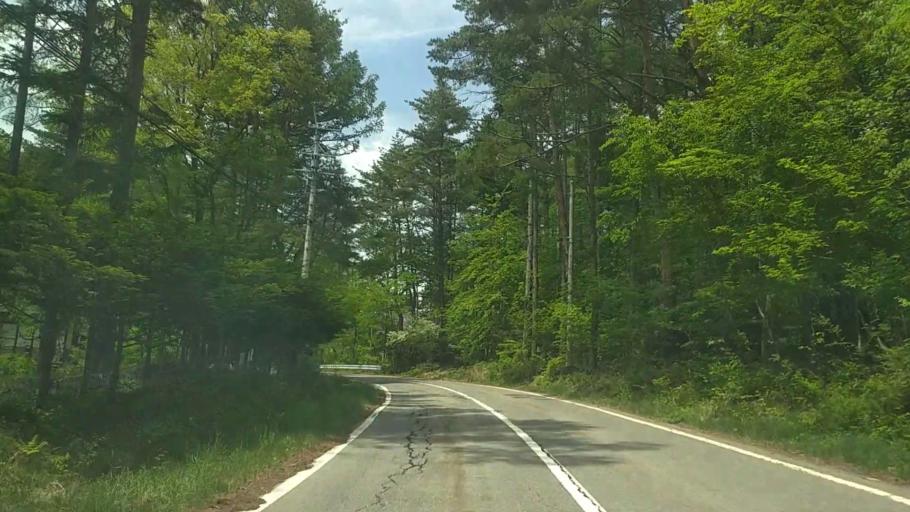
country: JP
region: Nagano
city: Saku
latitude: 36.1083
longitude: 138.4156
